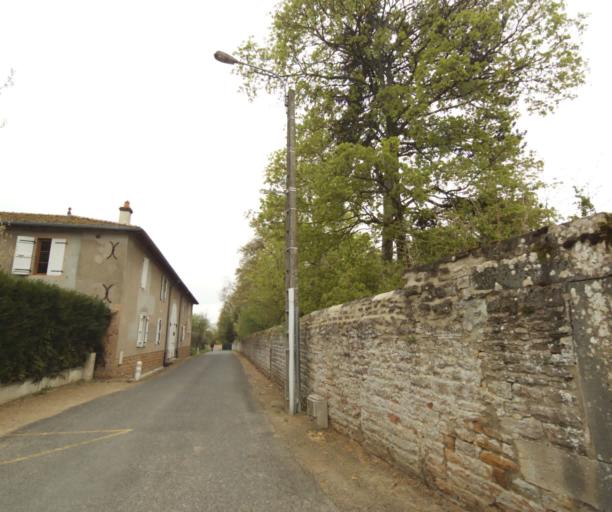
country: FR
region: Bourgogne
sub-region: Departement de Saone-et-Loire
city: Charnay-les-Macon
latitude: 46.2933
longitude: 4.7888
